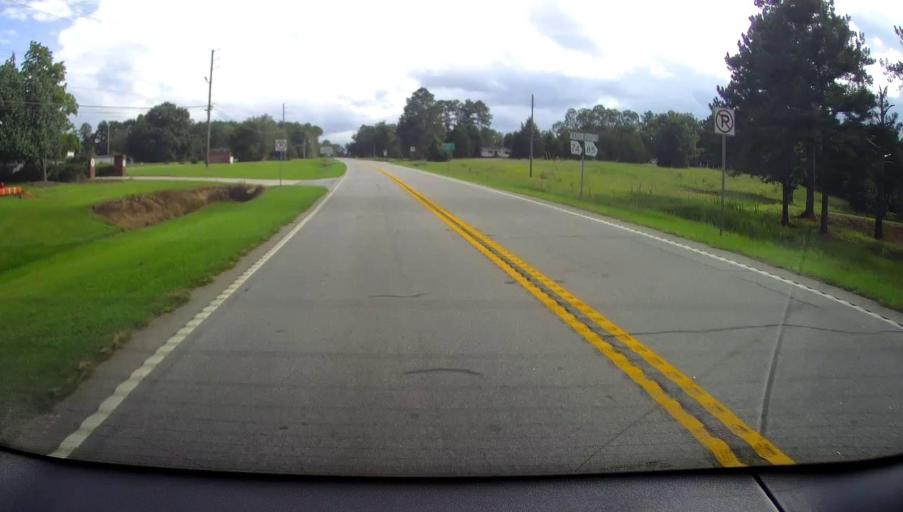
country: US
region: Georgia
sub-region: Meriwether County
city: Manchester
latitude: 32.9930
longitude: -84.5731
